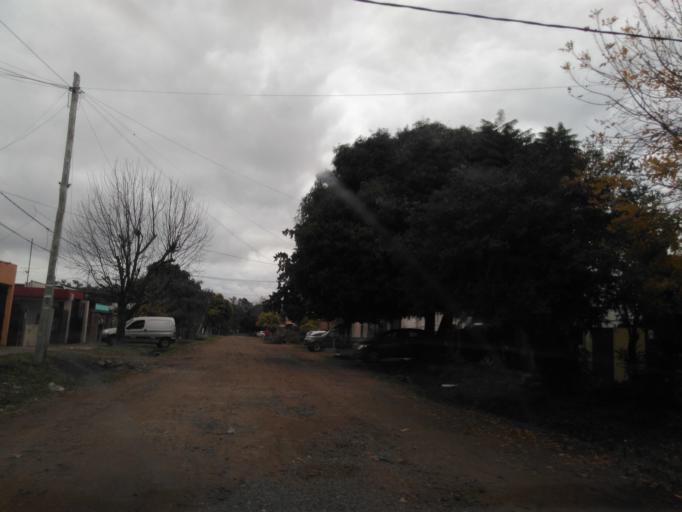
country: AR
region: Chaco
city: Fontana
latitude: -27.4361
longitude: -59.0161
